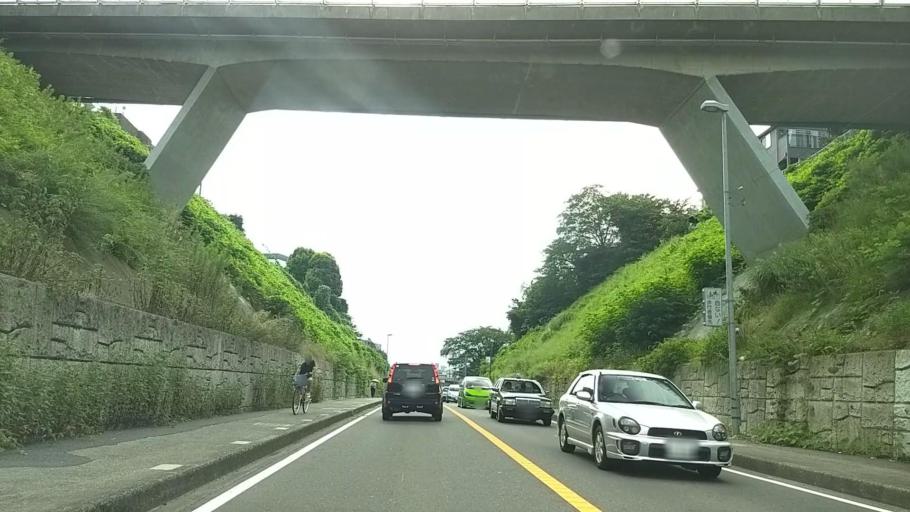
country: JP
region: Kanagawa
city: Zama
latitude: 35.4523
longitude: 139.4003
